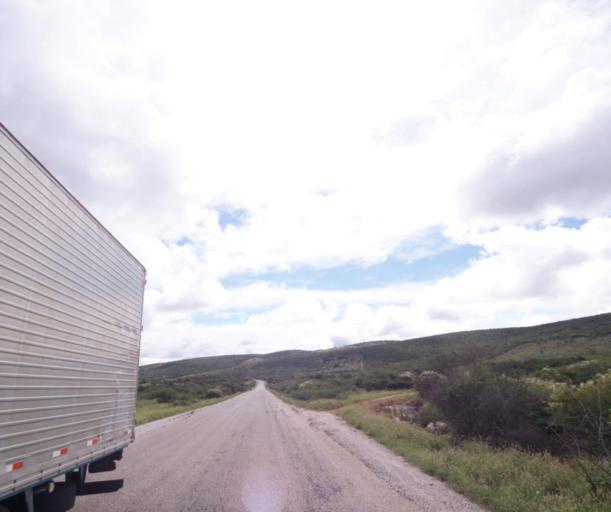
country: BR
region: Bahia
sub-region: Brumado
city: Brumado
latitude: -14.1979
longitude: -41.5910
